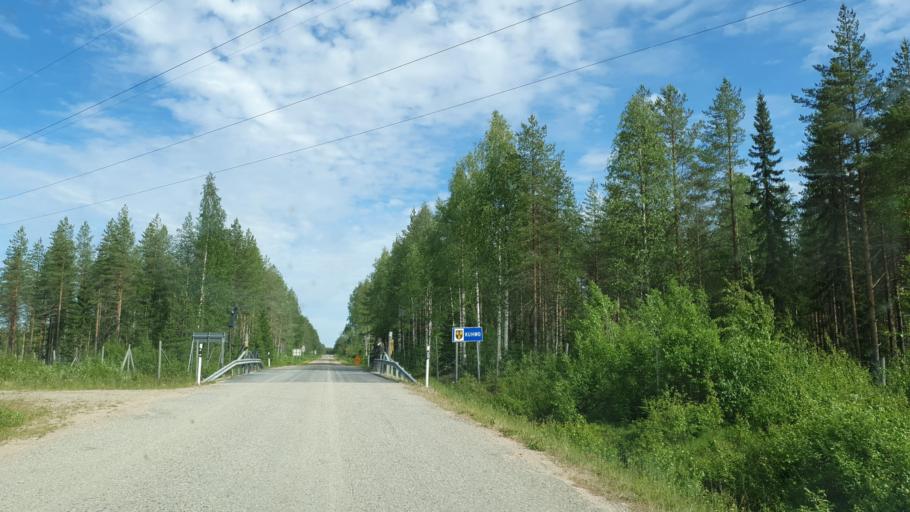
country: FI
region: Kainuu
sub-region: Kehys-Kainuu
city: Kuhmo
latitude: 64.5157
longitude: 29.3989
